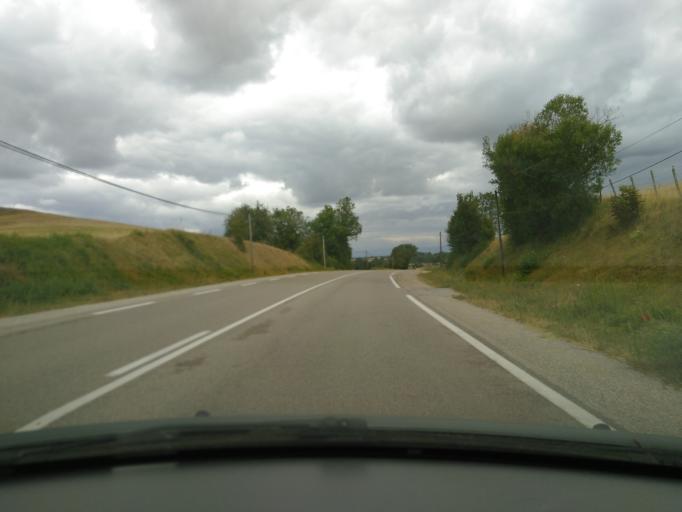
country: FR
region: Rhone-Alpes
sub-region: Departement de l'Isere
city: Champier
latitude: 45.4916
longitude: 5.2964
